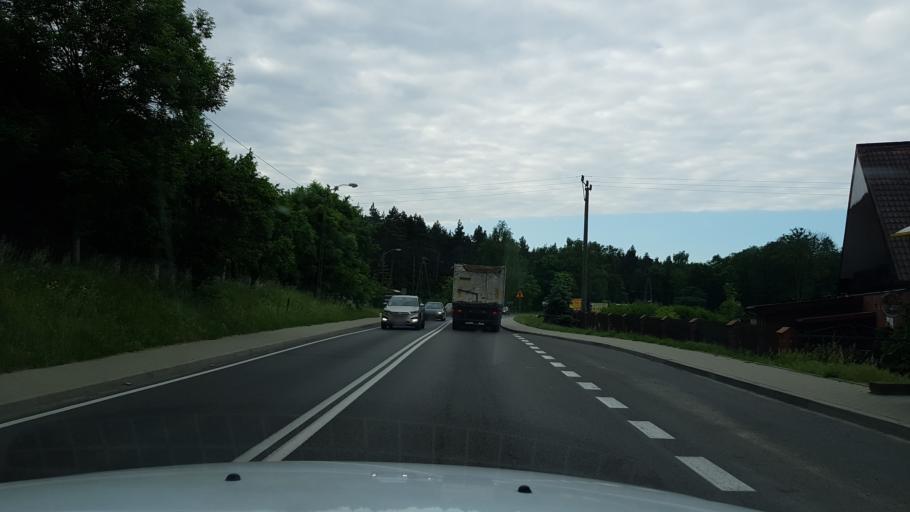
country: PL
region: West Pomeranian Voivodeship
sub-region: Powiat gryfinski
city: Gryfino
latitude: 53.2778
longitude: 14.5132
